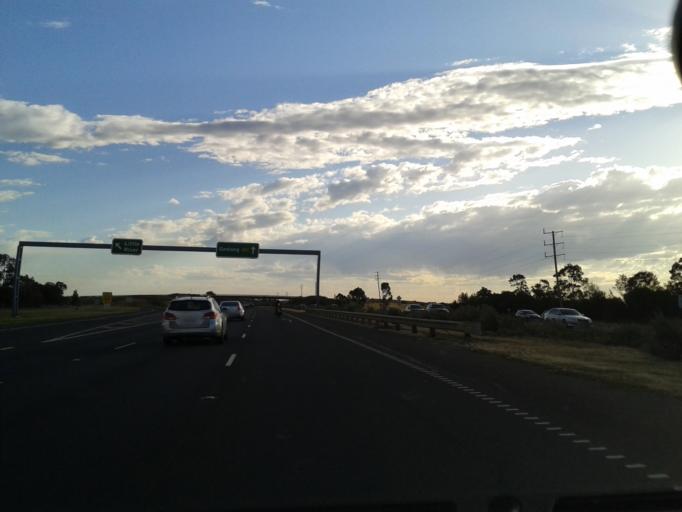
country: AU
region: Victoria
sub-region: Wyndham
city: Little River
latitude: -37.9651
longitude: 144.5639
